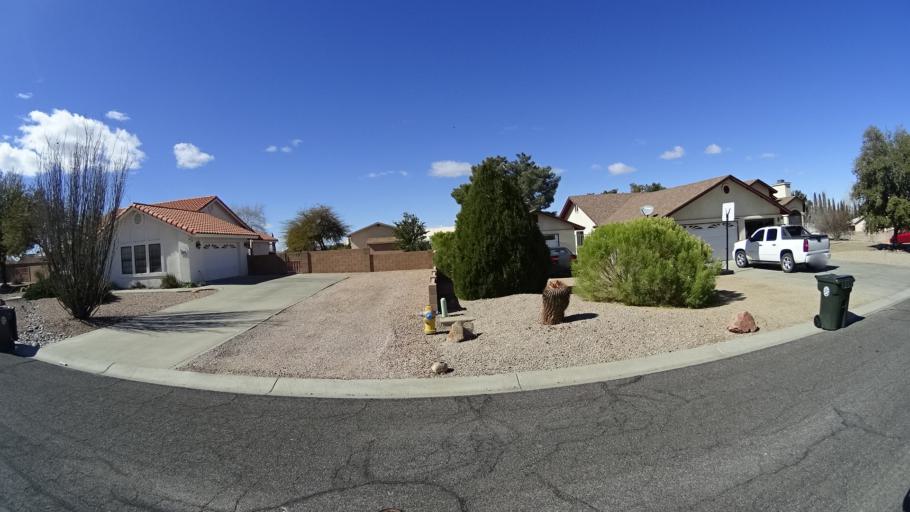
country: US
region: Arizona
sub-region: Mohave County
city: Kingman
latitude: 35.2003
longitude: -113.9733
